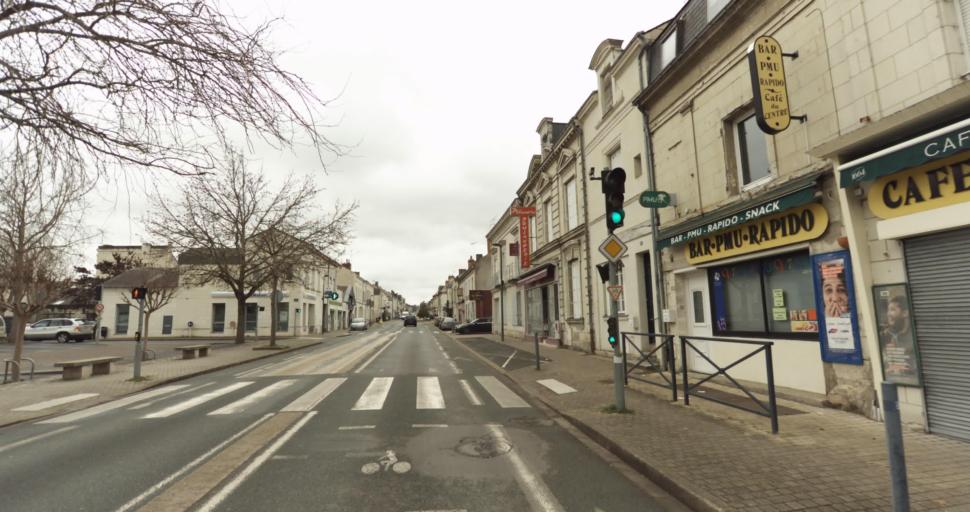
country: FR
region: Pays de la Loire
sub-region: Departement de Maine-et-Loire
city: Saumur
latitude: 47.2500
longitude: -0.0897
